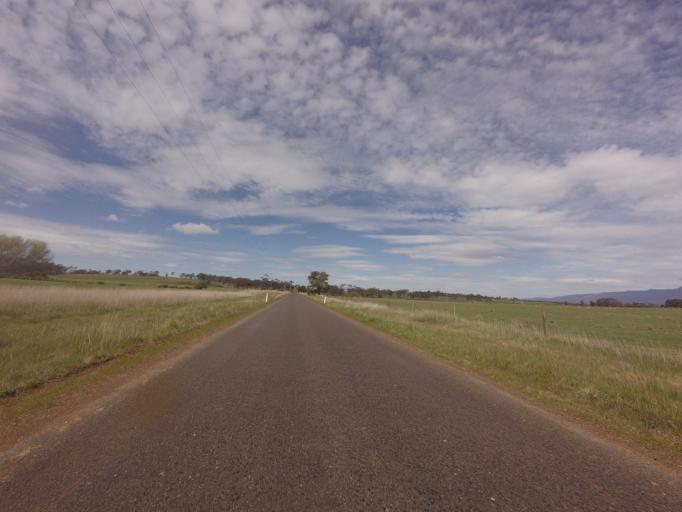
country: AU
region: Tasmania
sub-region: Northern Midlands
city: Longford
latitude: -41.7787
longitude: 147.2290
